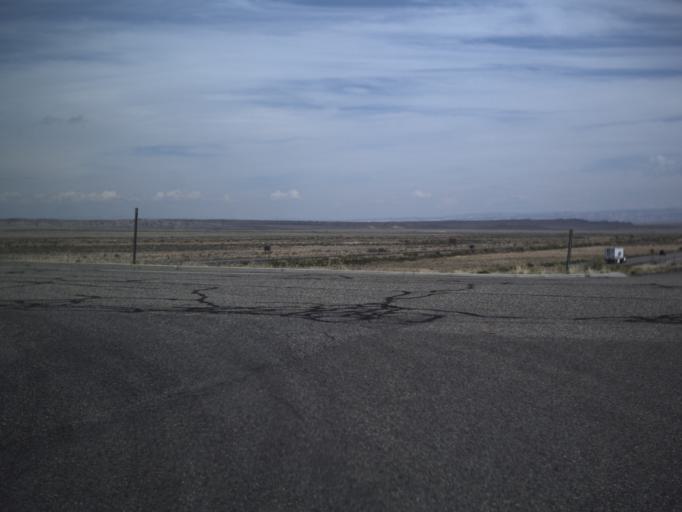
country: US
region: Utah
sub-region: Grand County
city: Moab
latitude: 38.9413
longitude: -109.6150
